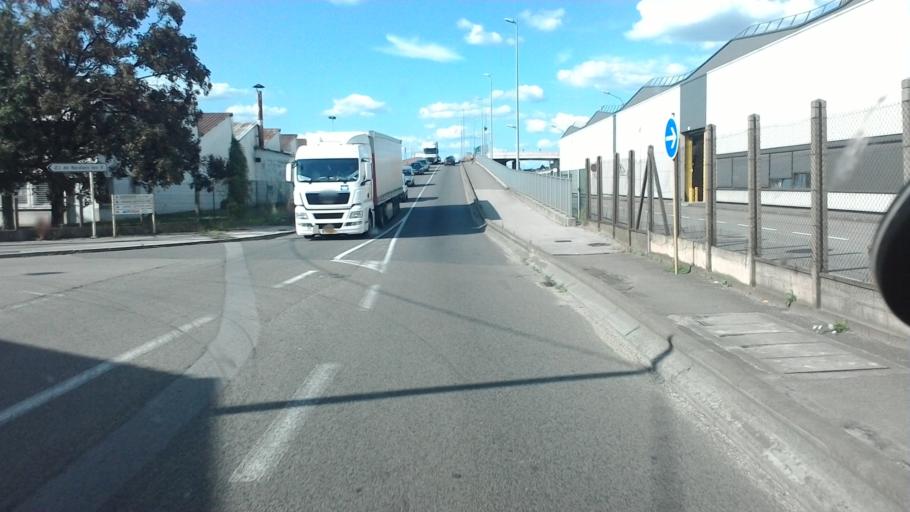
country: FR
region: Franche-Comte
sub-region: Departement de la Haute-Saone
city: Noidans-les-Vesoul
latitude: 47.6182
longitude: 6.1348
